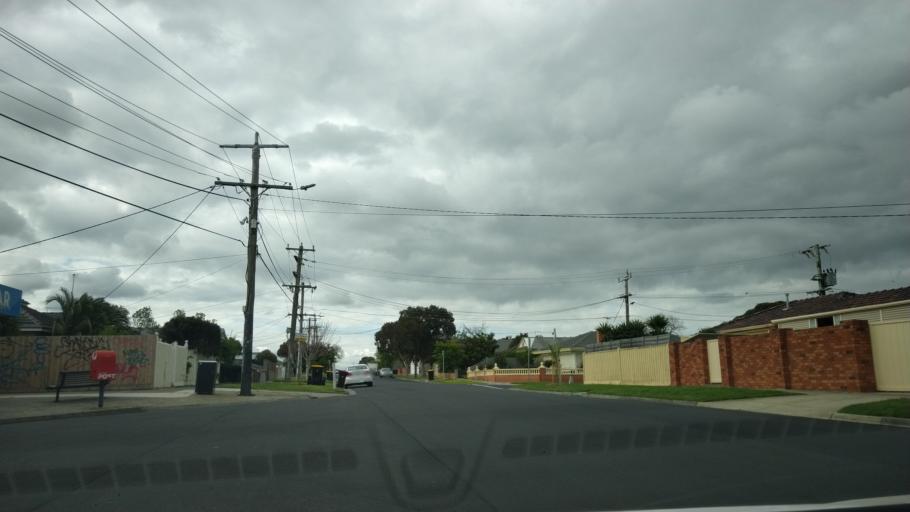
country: AU
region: Victoria
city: Highett
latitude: -37.9579
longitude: 145.0664
